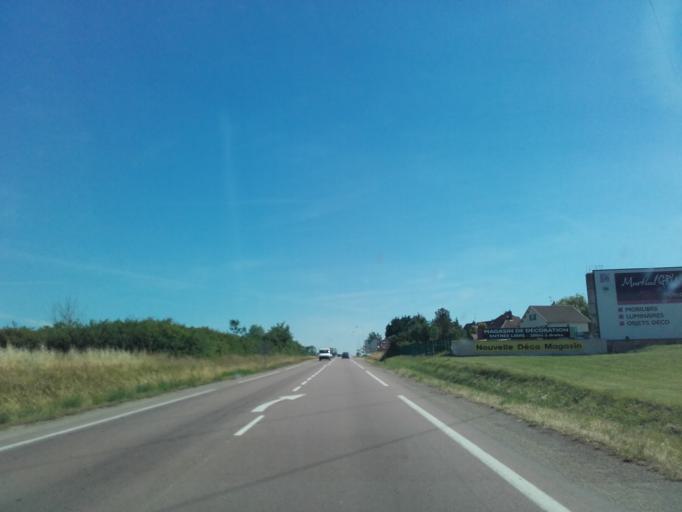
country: FR
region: Bourgogne
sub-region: Departement de la Cote-d'Or
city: Corpeau
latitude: 46.9340
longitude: 4.7526
